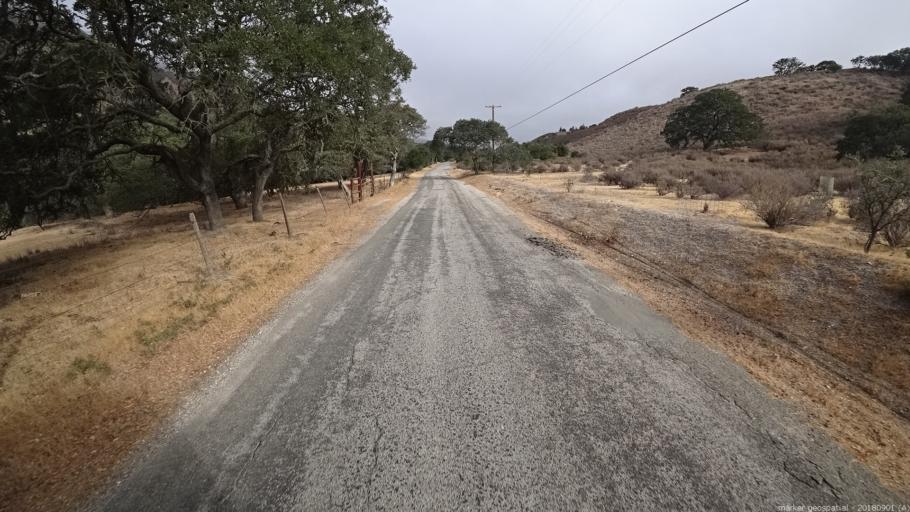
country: US
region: California
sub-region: Monterey County
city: Greenfield
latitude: 36.2655
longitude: -121.2973
